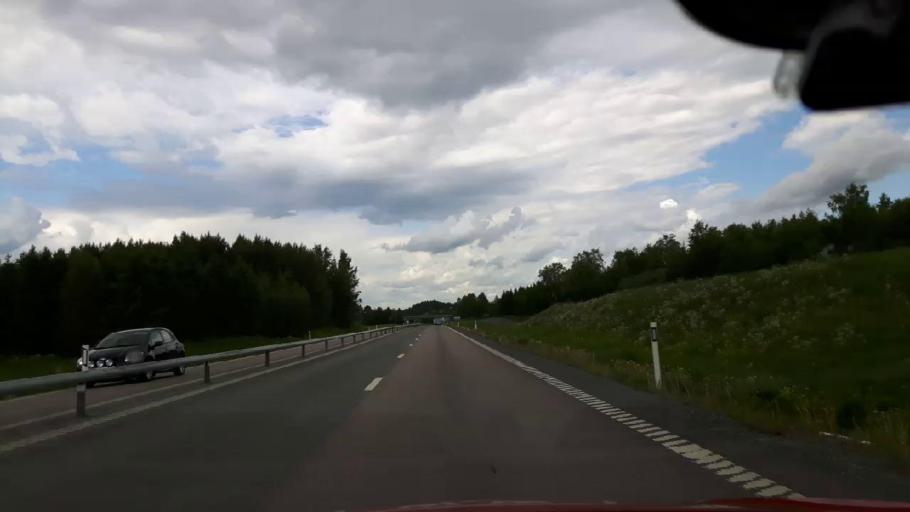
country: SE
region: Jaemtland
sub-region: Krokoms Kommun
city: Krokom
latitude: 63.3014
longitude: 14.4942
